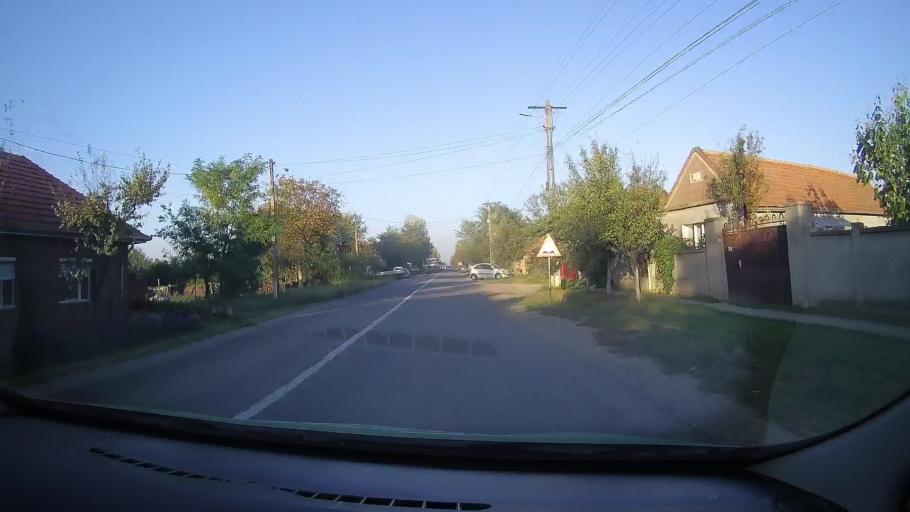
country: RO
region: Bihor
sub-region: Comuna Biharea
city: Biharea
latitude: 47.1661
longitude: 21.9497
